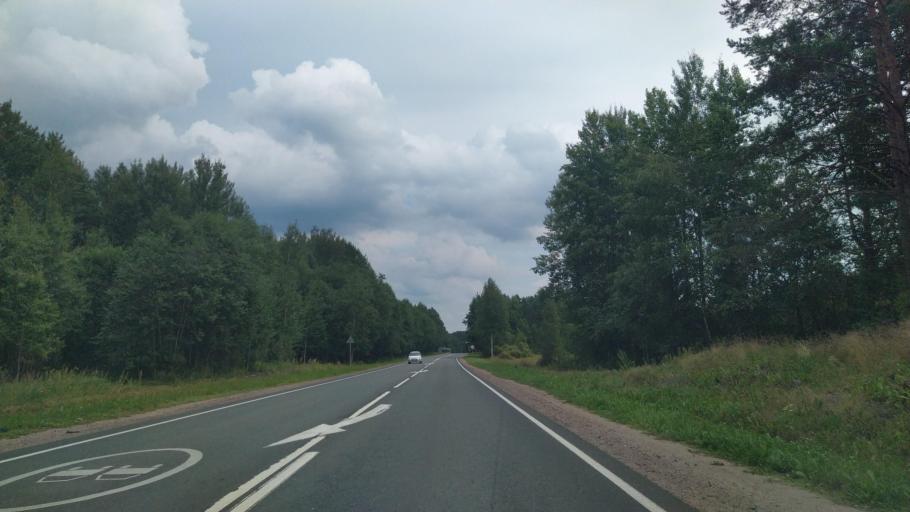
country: RU
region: Pskov
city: Pskov
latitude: 57.8333
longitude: 28.5227
